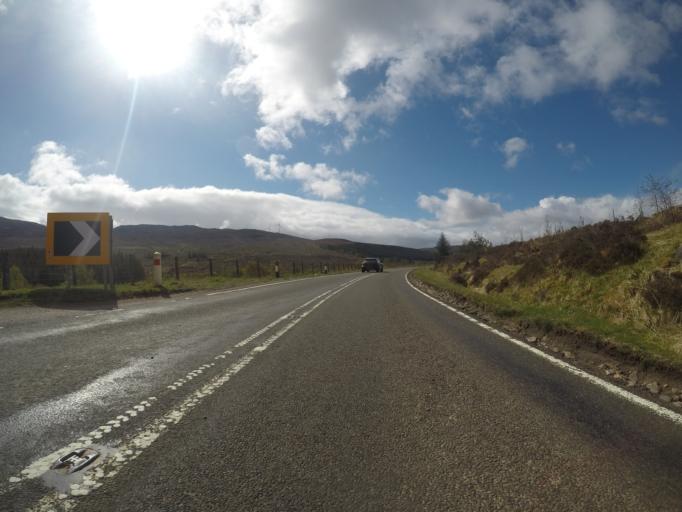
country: GB
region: Scotland
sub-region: Highland
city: Spean Bridge
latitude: 57.1411
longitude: -4.9520
